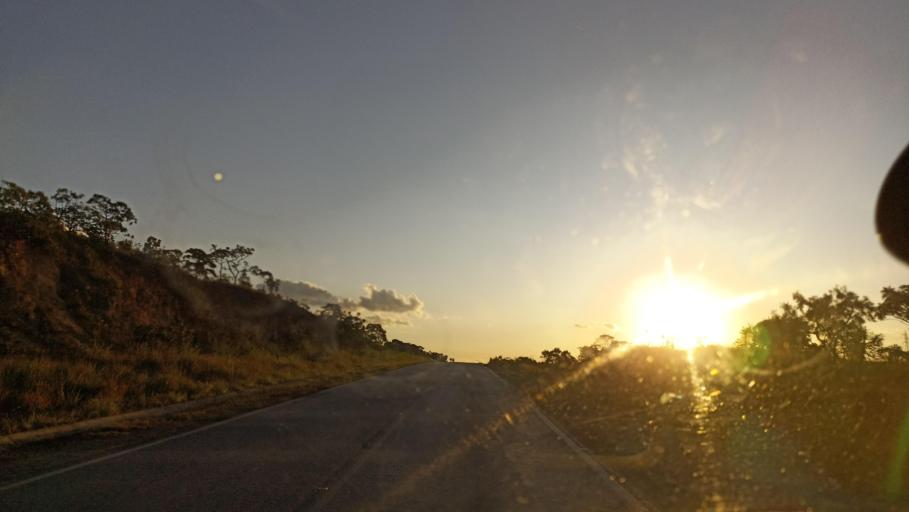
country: BR
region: Minas Gerais
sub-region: Sao Joao Del Rei
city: Sao Joao del Rei
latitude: -21.2250
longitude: -44.3646
